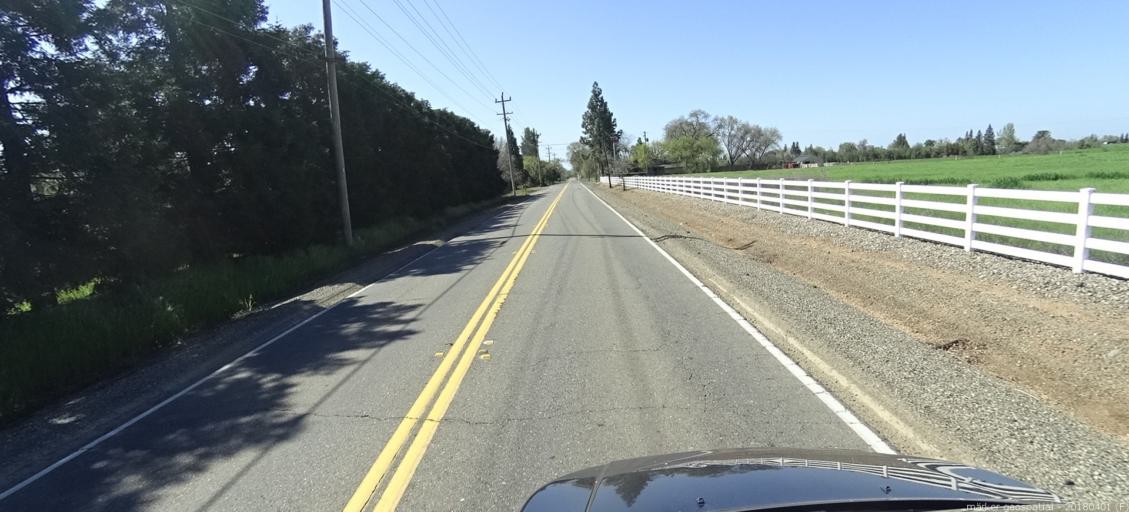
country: US
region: California
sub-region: Sacramento County
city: Wilton
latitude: 38.4540
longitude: -121.1829
